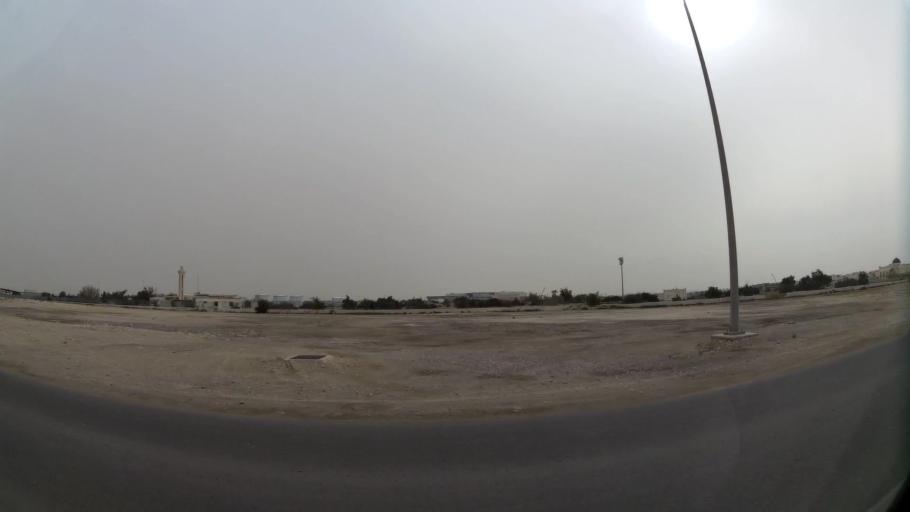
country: QA
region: Baladiyat ad Dawhah
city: Doha
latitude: 25.2414
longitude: 51.5137
